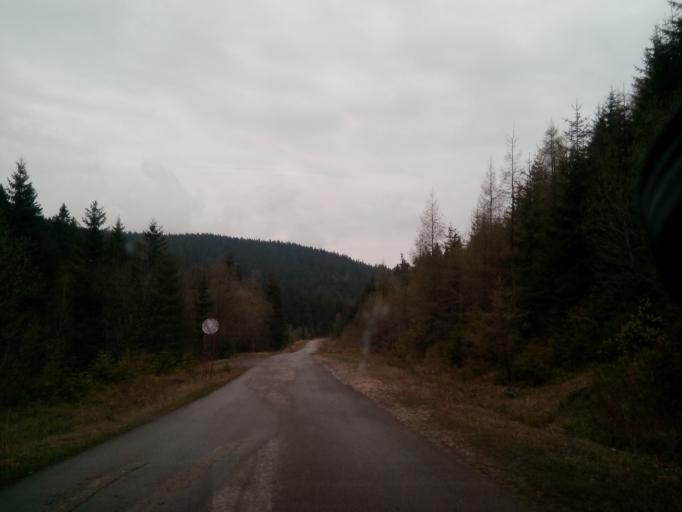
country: SK
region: Zilinsky
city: Oravska Lesna
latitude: 49.3205
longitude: 19.1875
